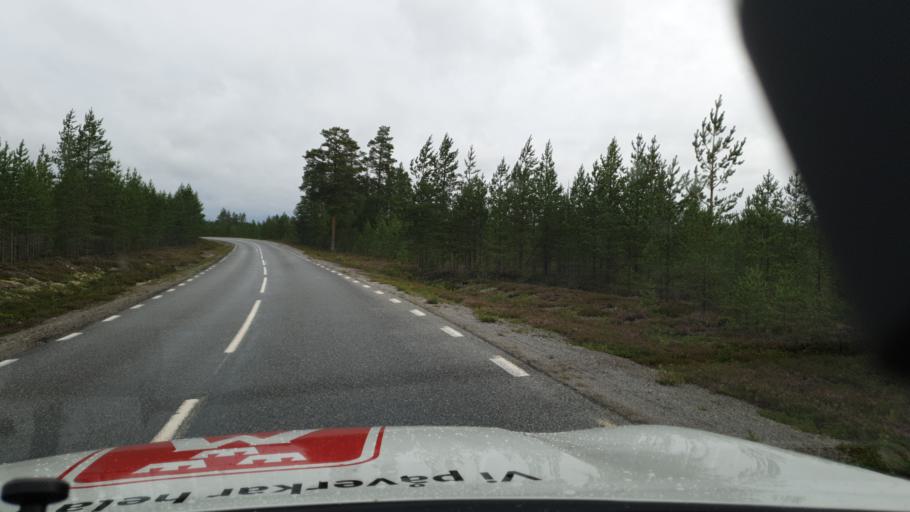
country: SE
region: Vaesterbotten
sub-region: Umea Kommun
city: Saevar
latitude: 63.9346
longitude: 20.5302
